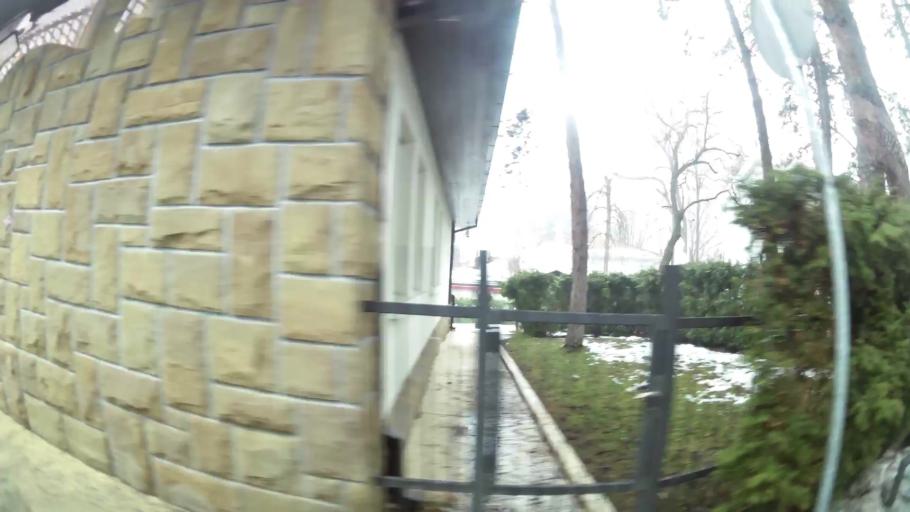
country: RS
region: Central Serbia
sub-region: Belgrade
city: Savski Venac
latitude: 44.7777
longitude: 20.4635
